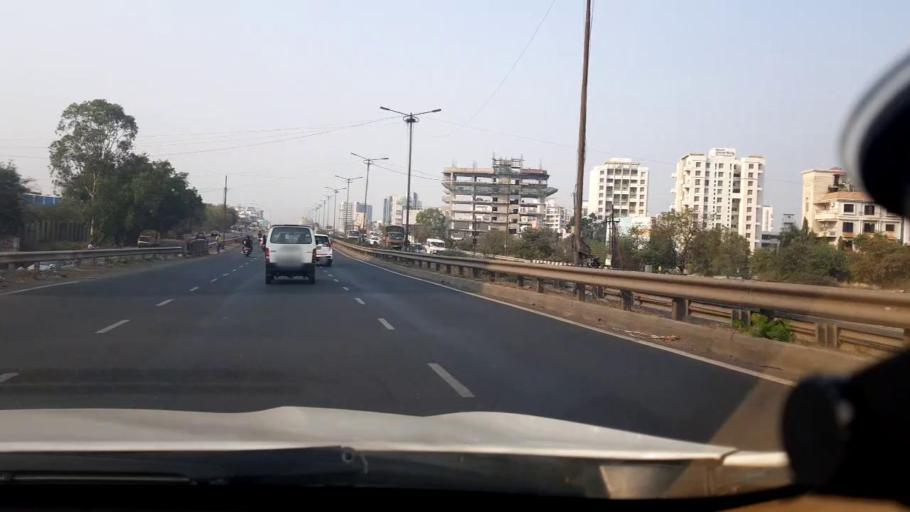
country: IN
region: Maharashtra
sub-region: Pune Division
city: Pimpri
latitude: 18.5569
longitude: 73.7700
